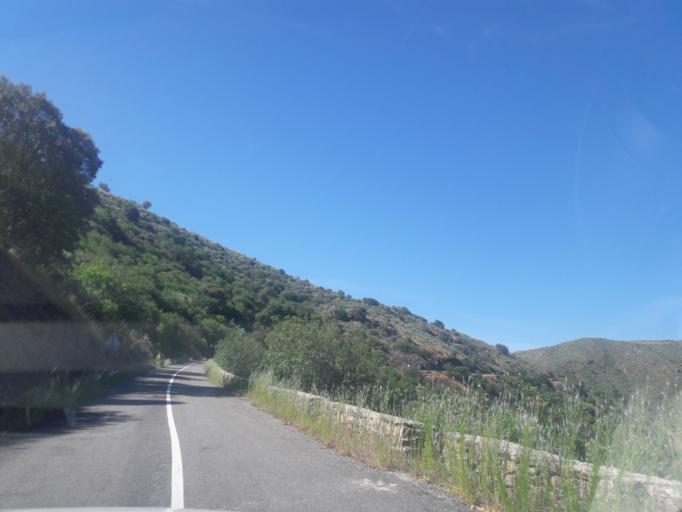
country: ES
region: Castille and Leon
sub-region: Provincia de Salamanca
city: Saucelle
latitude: 41.0235
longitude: -6.7487
